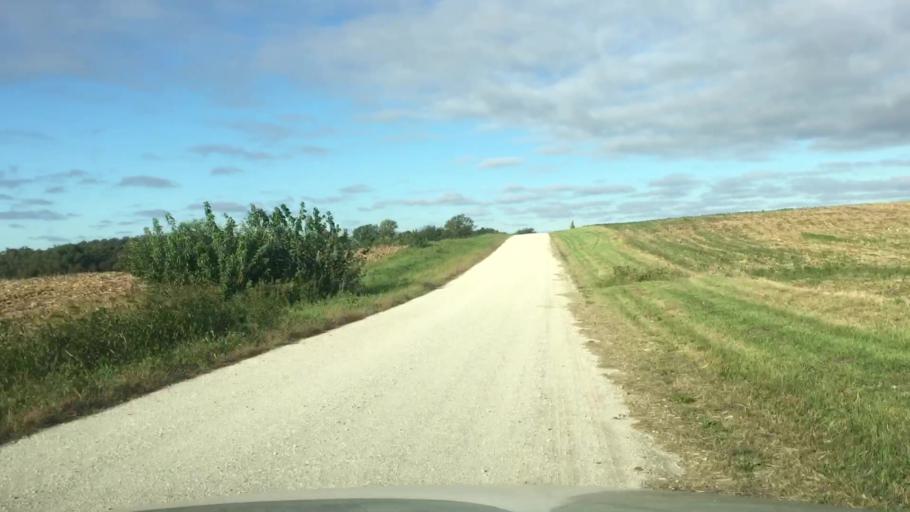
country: US
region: Missouri
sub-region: Howard County
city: New Franklin
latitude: 39.0791
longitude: -92.7470
